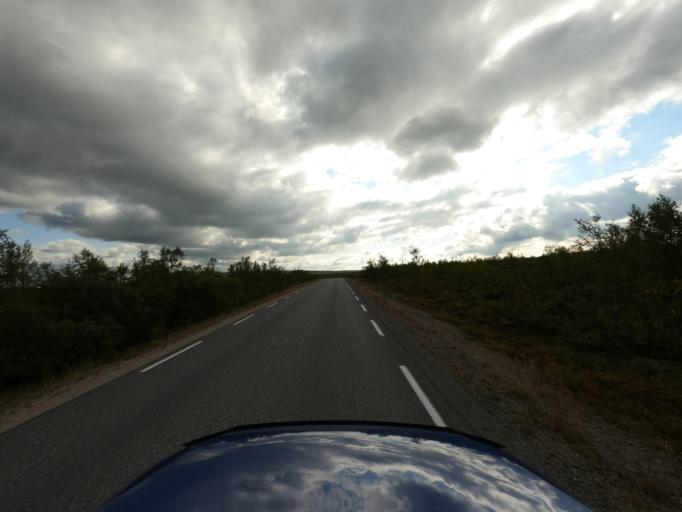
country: NO
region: Finnmark Fylke
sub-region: Porsanger
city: Lakselv
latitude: 69.3702
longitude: 24.2792
